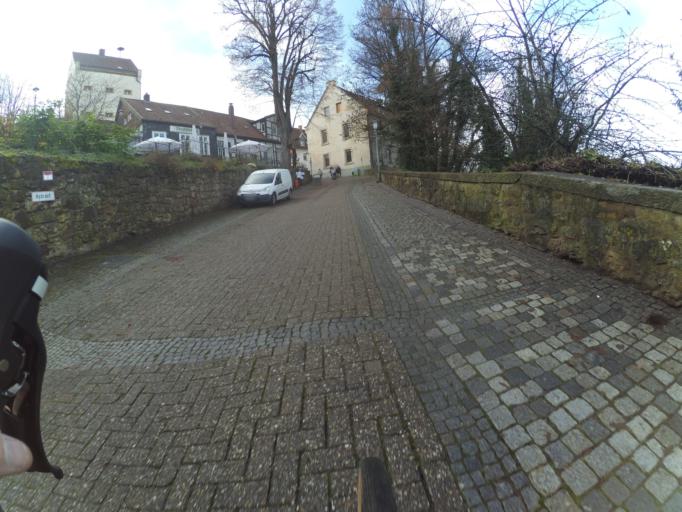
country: DE
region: North Rhine-Westphalia
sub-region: Regierungsbezirk Munster
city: Tecklenburg
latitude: 52.2203
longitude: 7.8098
